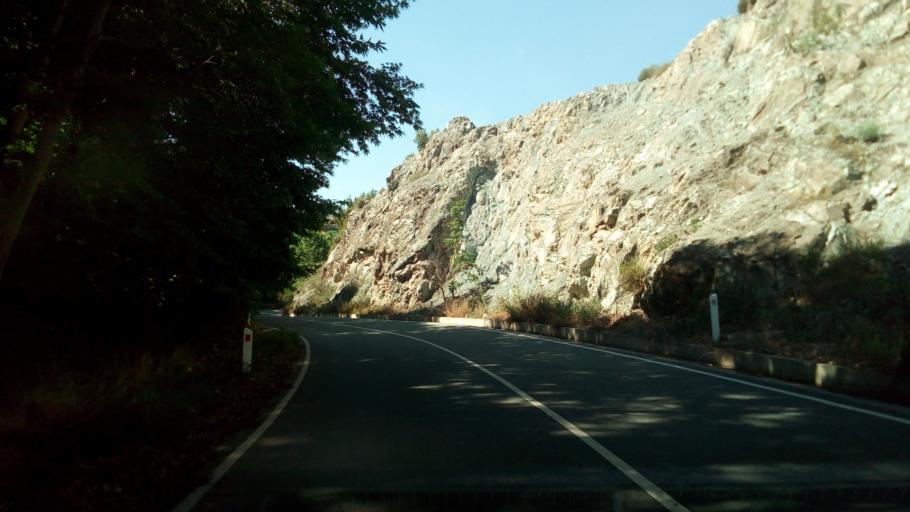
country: CY
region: Limassol
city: Pachna
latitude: 34.7988
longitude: 32.7053
